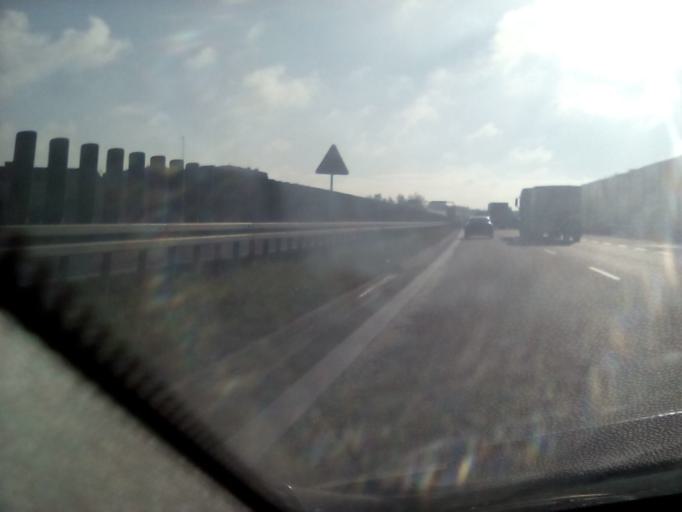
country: PL
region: Masovian Voivodeship
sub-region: Powiat grojecki
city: Grojec
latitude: 51.8598
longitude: 20.8559
